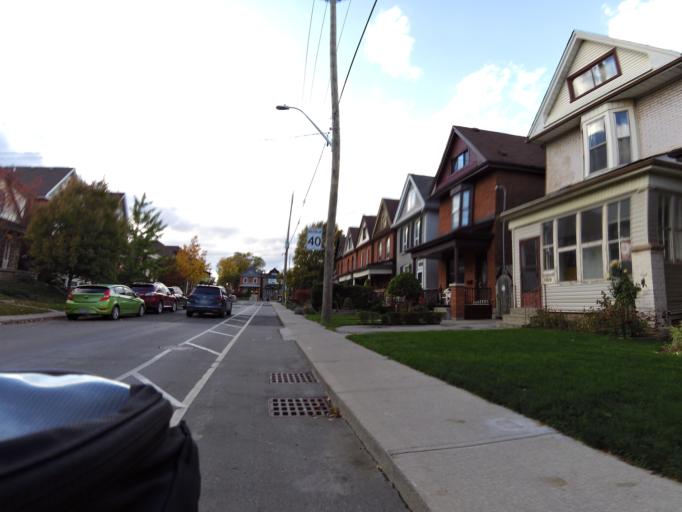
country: CA
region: Ontario
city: Hamilton
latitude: 43.2542
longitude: -79.8901
